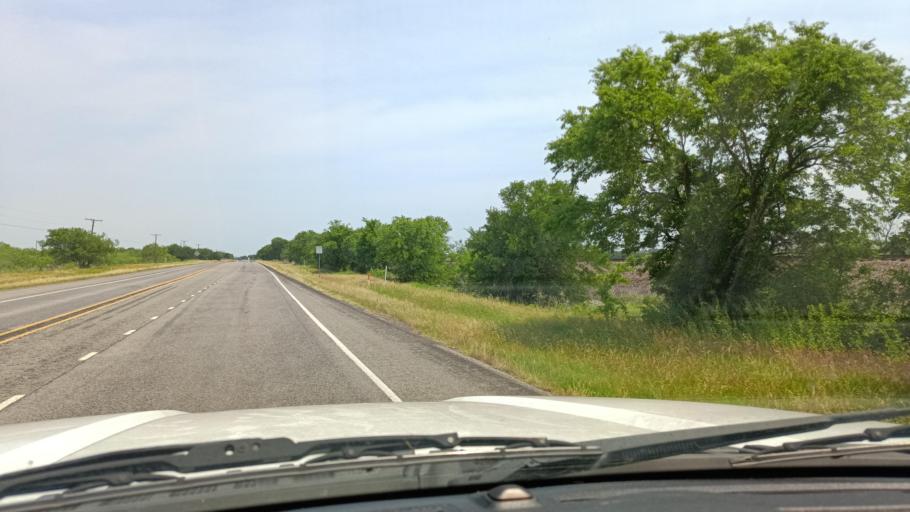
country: US
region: Texas
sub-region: Bell County
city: Rogers
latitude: 30.8679
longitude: -97.1182
